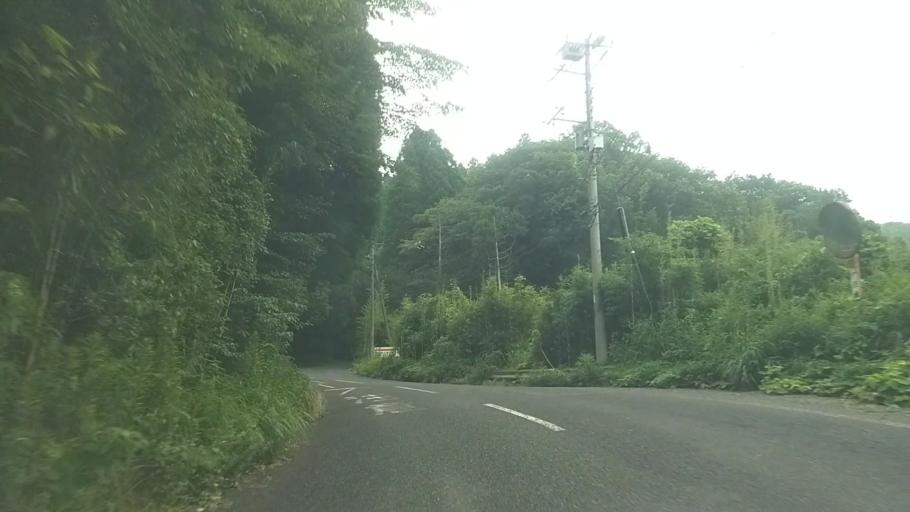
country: JP
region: Chiba
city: Kimitsu
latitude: 35.2373
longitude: 139.9873
